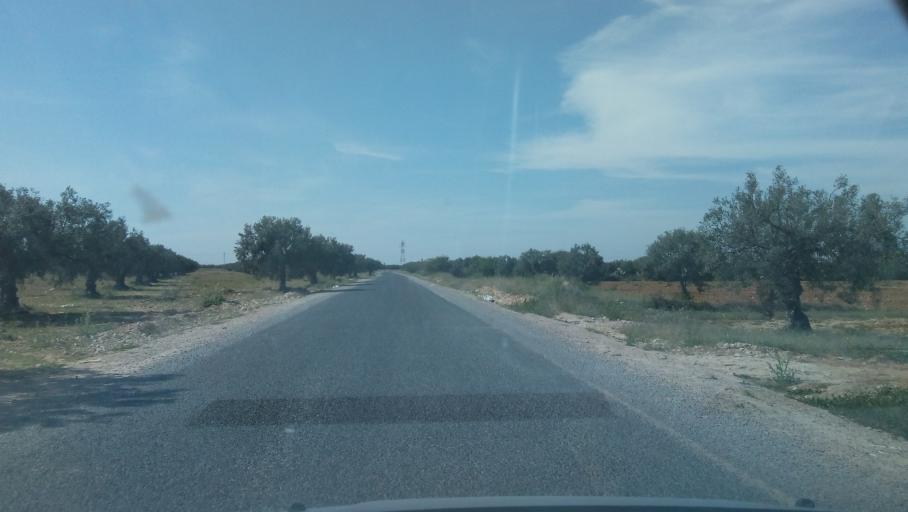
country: TN
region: Safaqis
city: Al Qarmadah
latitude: 34.8771
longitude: 10.8740
